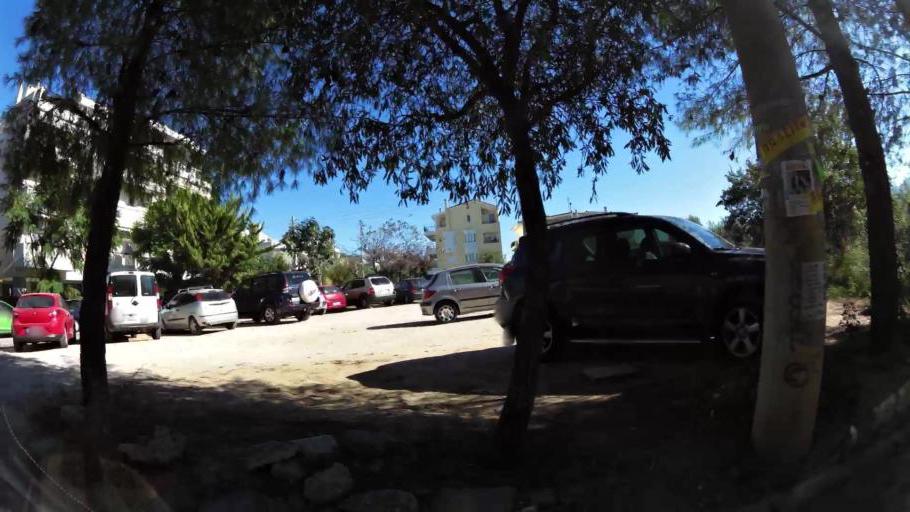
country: GR
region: Attica
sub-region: Nomarchia Athinas
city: Vrilissia
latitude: 38.0231
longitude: 23.8189
